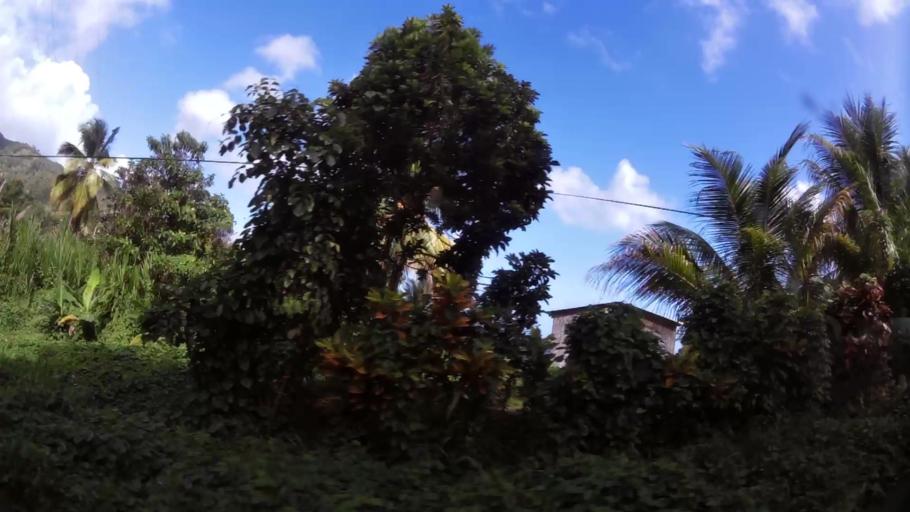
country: DM
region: Saint David
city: Castle Bruce
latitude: 15.4727
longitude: -61.2492
